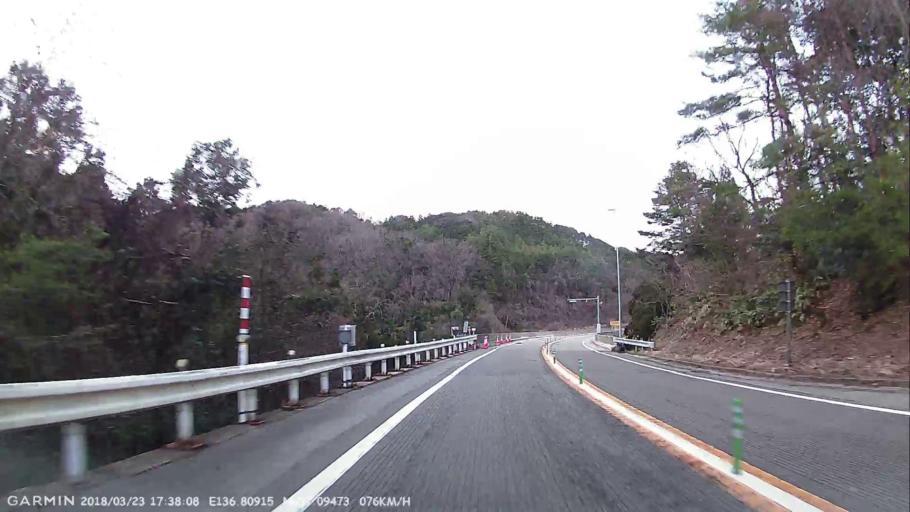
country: JP
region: Ishikawa
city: Nanao
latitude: 37.0949
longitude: 136.8092
